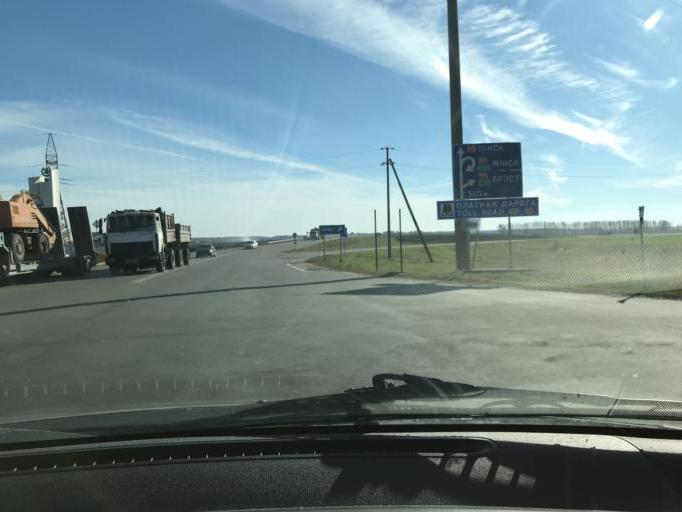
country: BY
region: Brest
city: Ivatsevichy
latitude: 52.7035
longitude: 25.3601
